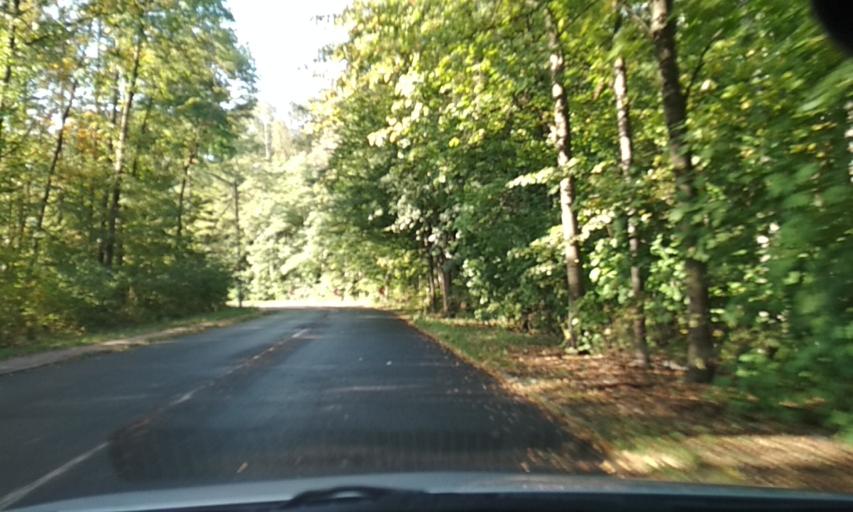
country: PL
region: Silesian Voivodeship
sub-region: Powiat bierunsko-ledzinski
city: Ledziny
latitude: 50.1705
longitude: 19.1564
